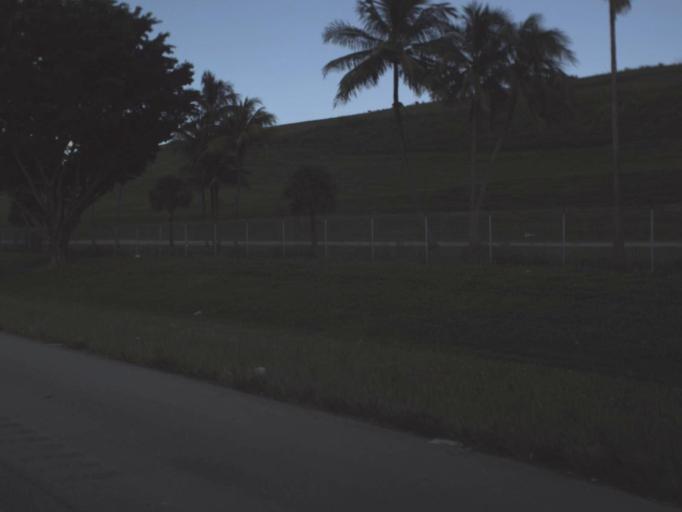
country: US
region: Florida
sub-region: Broward County
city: Coconut Creek
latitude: 26.2808
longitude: -80.1689
